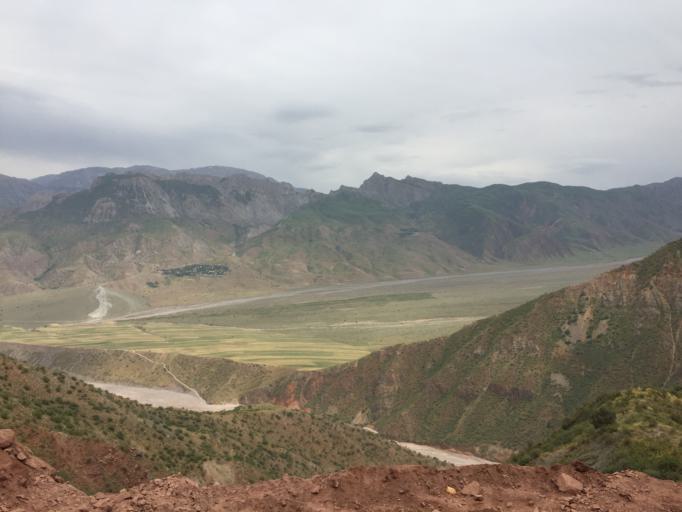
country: AF
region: Badakhshan
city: Deh Khwahan
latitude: 37.8080
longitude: 70.1606
